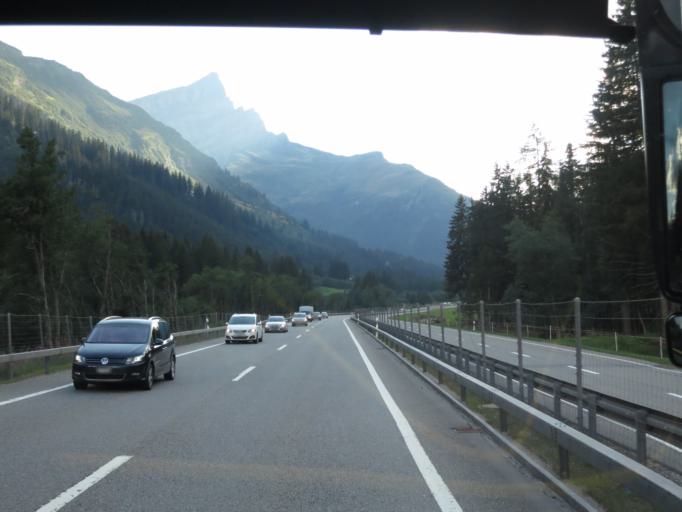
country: CH
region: Grisons
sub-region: Hinterrhein District
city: Hinterrhein
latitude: 46.5432
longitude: 9.2804
